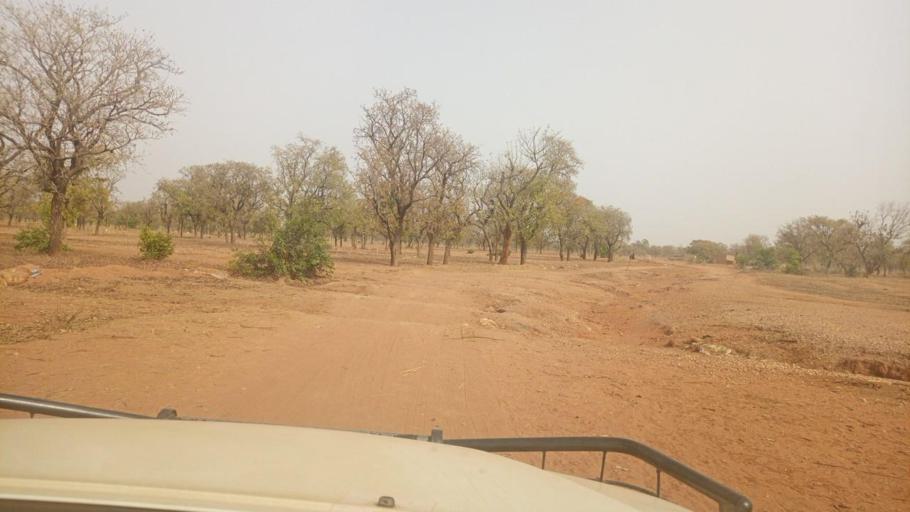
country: BF
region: Boucle du Mouhoun
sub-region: Province des Banwa
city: Salanso
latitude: 12.0955
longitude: -4.3305
